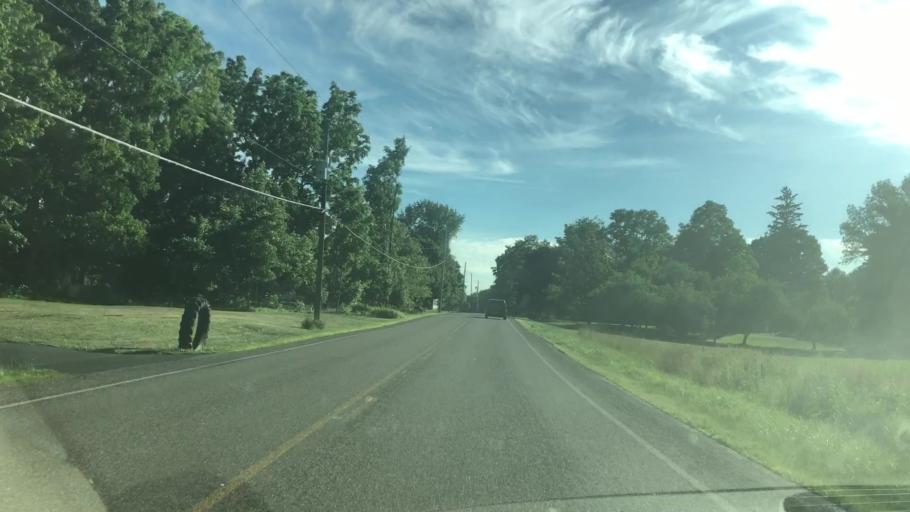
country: US
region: New York
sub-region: Wayne County
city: Macedon
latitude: 43.0515
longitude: -77.3325
